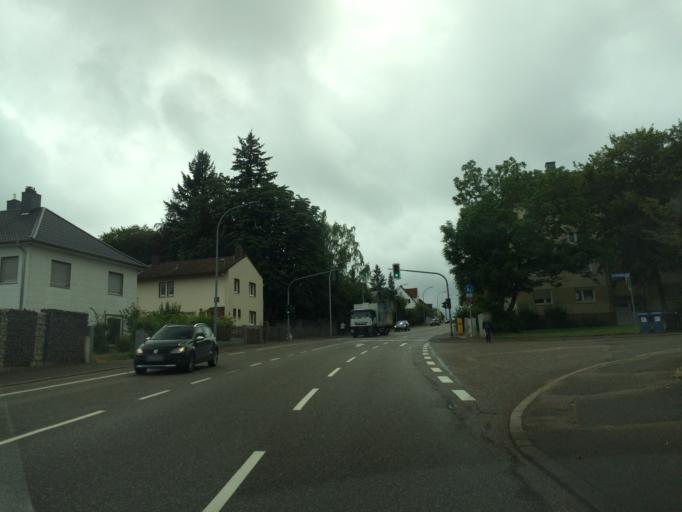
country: DE
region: Rheinland-Pfalz
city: Pirmasens
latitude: 49.1878
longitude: 7.6246
